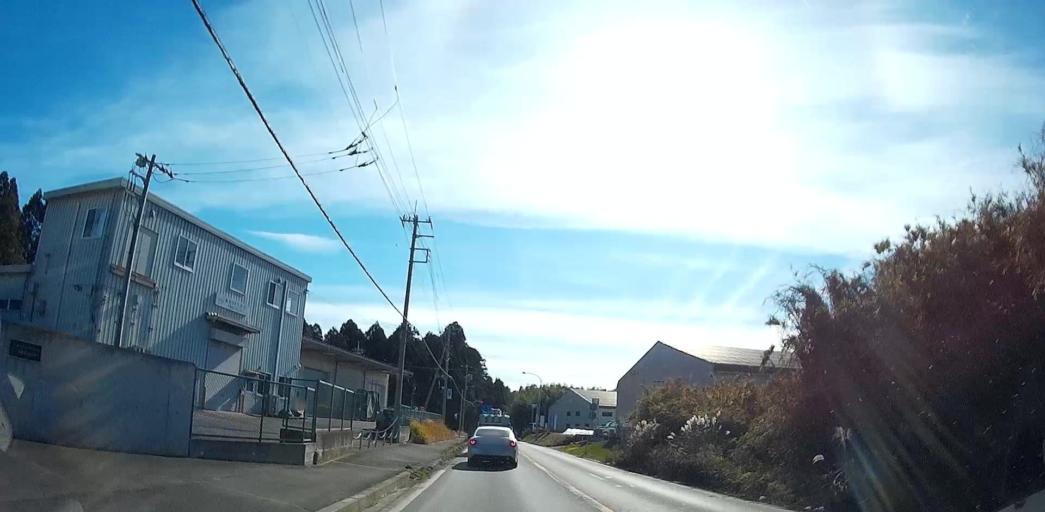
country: JP
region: Chiba
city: Yokaichiba
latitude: 35.7508
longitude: 140.4570
